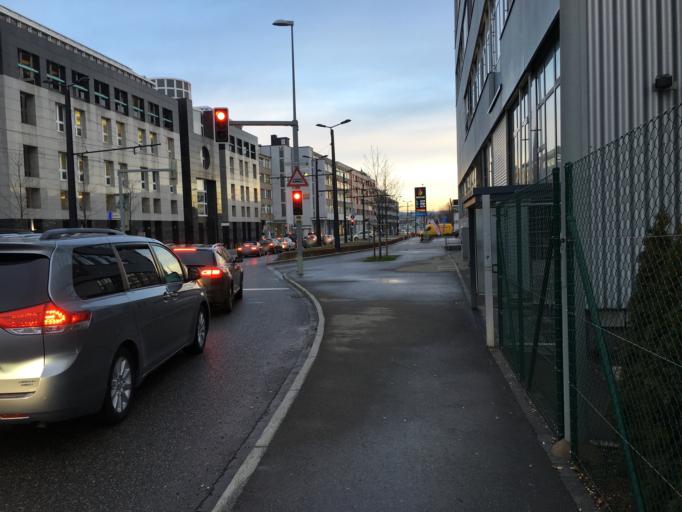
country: CH
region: Zurich
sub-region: Bezirk Uster
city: Duebendorf / Wasserfurren
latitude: 47.3977
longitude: 8.6046
